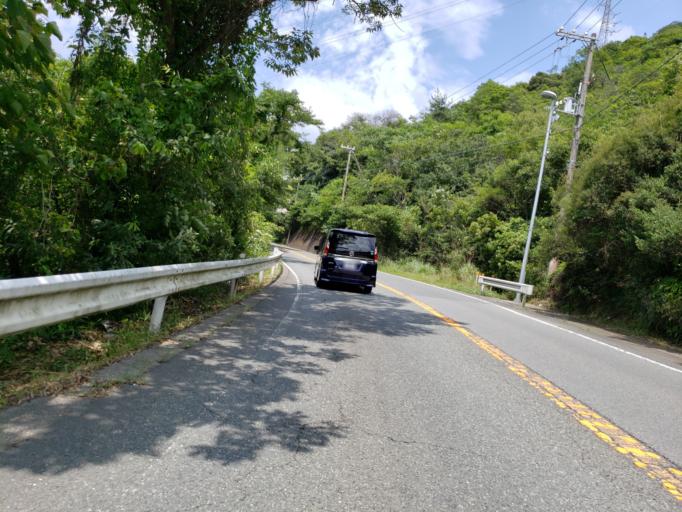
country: JP
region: Hyogo
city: Aioi
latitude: 34.7819
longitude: 134.4373
